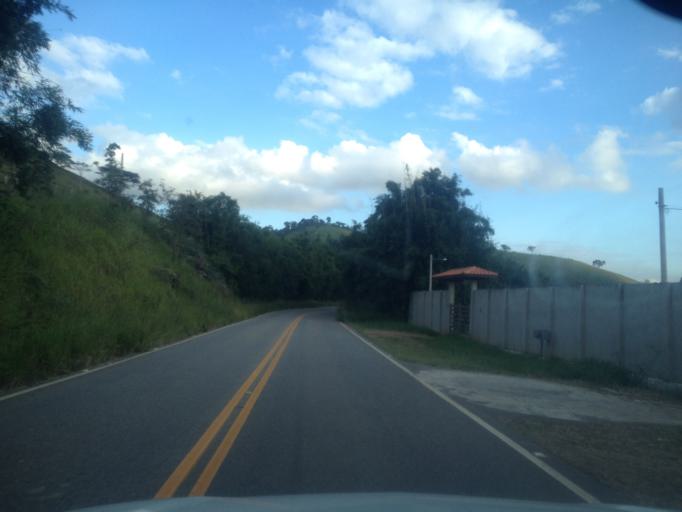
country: BR
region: Rio de Janeiro
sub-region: Quatis
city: Quatis
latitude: -22.3632
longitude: -44.2560
